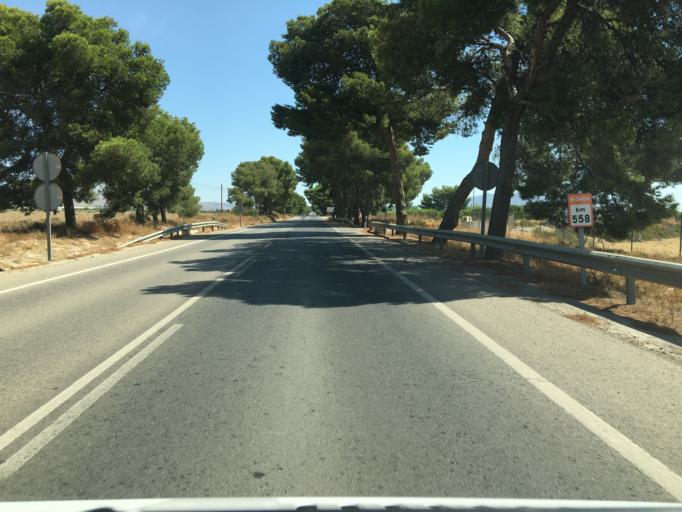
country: ES
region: Andalusia
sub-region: Provincia de Almeria
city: Huercal-Overa
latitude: 37.4188
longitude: -1.9226
